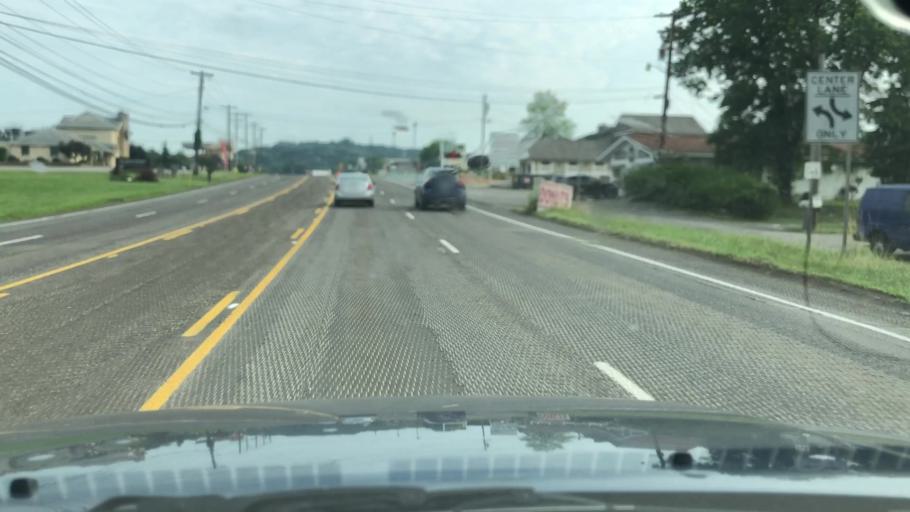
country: US
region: Pennsylvania
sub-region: Butler County
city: Nixon
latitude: 40.7581
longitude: -79.9239
